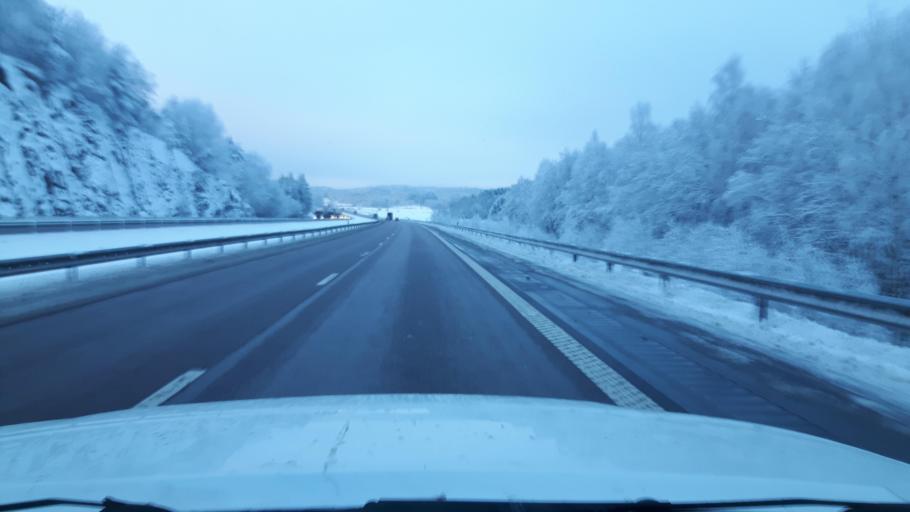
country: SE
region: Halland
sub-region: Kungsbacka Kommun
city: Frillesas
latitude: 57.3563
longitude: 12.2098
